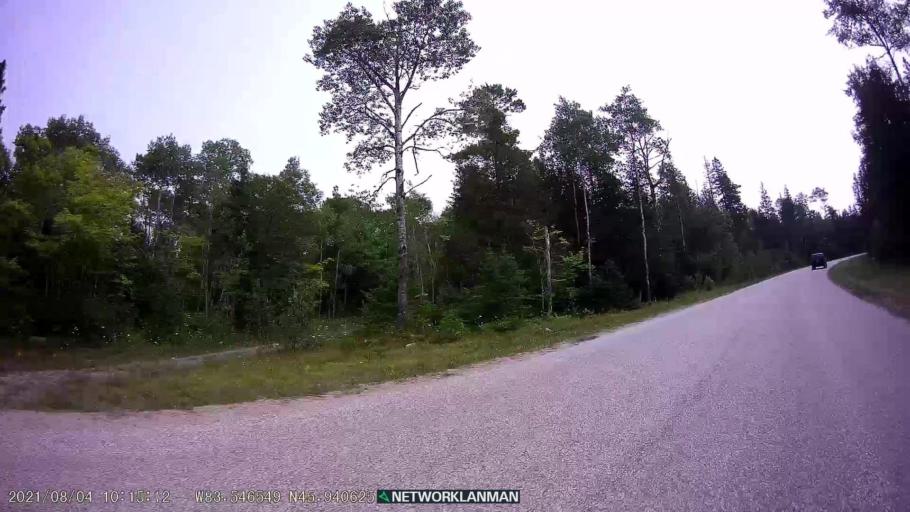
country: CA
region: Ontario
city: Thessalon
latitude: 45.9405
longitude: -83.5462
